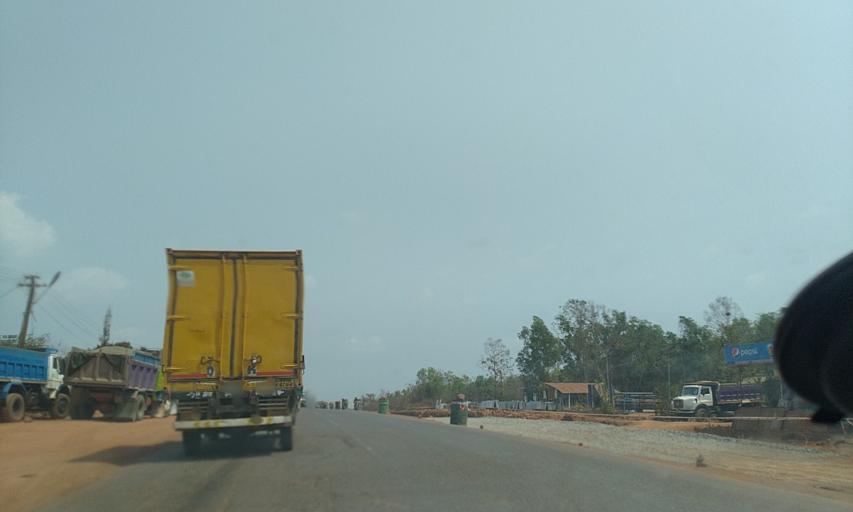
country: IN
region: Goa
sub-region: North Goa
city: Pernem
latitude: 15.6880
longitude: 73.8294
